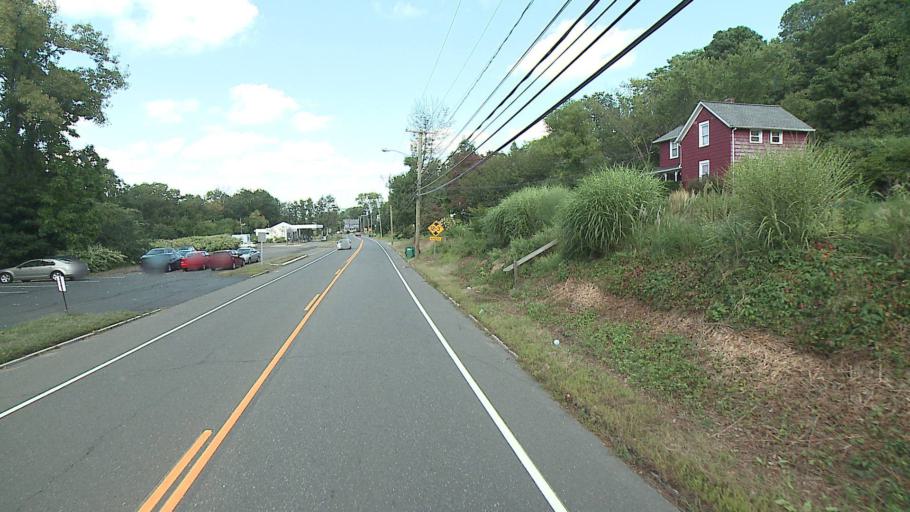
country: US
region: Connecticut
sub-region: New Haven County
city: Seymour
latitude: 41.3856
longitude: -73.0743
